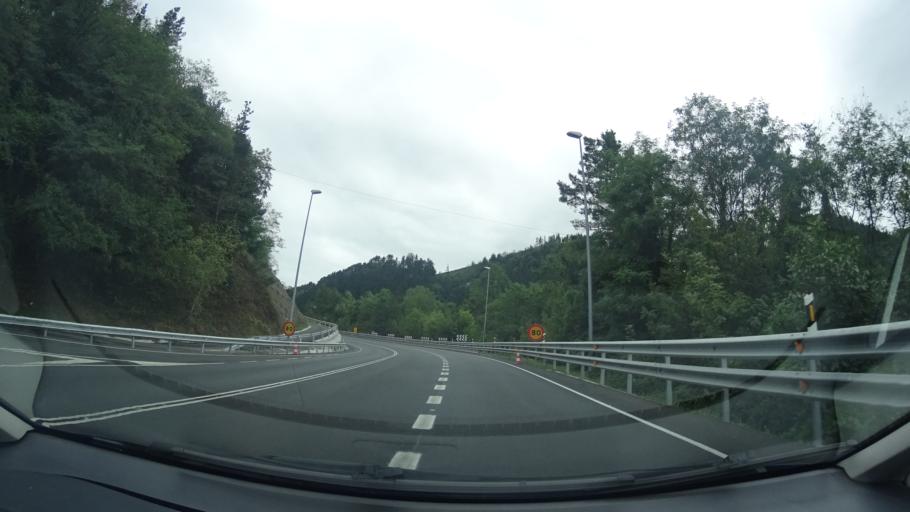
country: ES
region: Basque Country
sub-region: Bizkaia
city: Zeanuri
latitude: 43.0921
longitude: -2.7491
